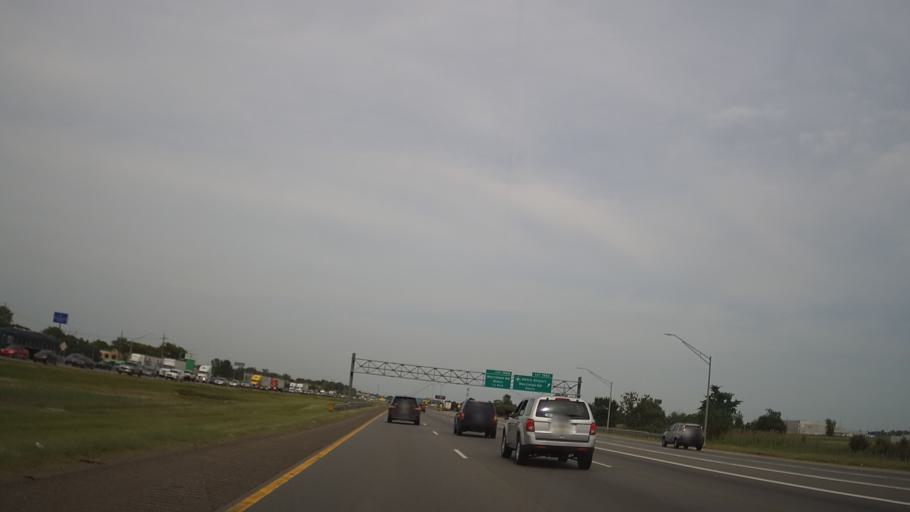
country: US
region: Michigan
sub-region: Wayne County
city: Romulus
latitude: 42.2367
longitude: -83.3501
